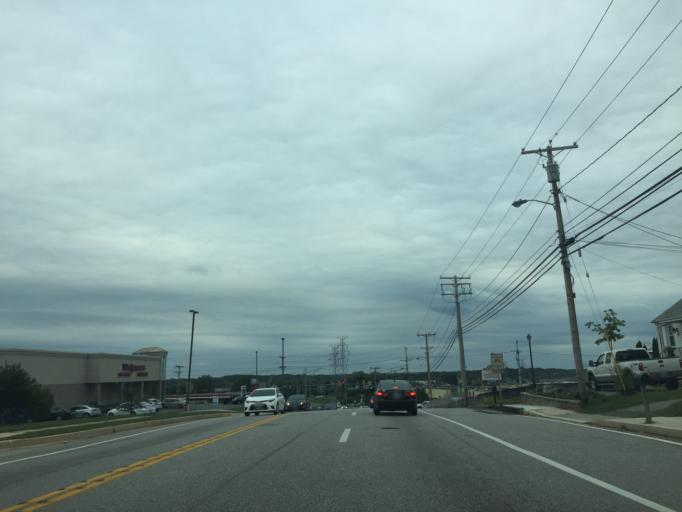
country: US
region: Maryland
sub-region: Baltimore County
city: Rossville
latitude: 39.3343
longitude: -76.4972
